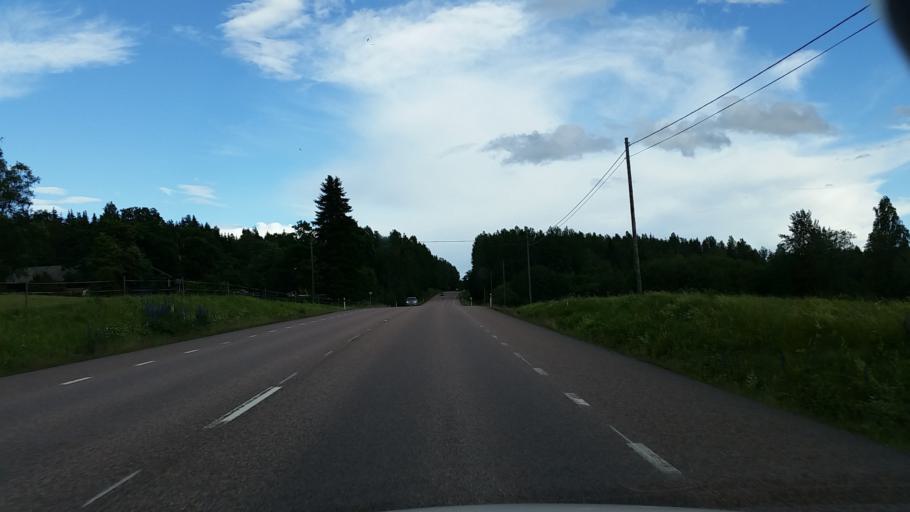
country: SE
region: Dalarna
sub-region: Ludvika Kommun
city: Ludvika
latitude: 60.1495
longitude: 15.2706
